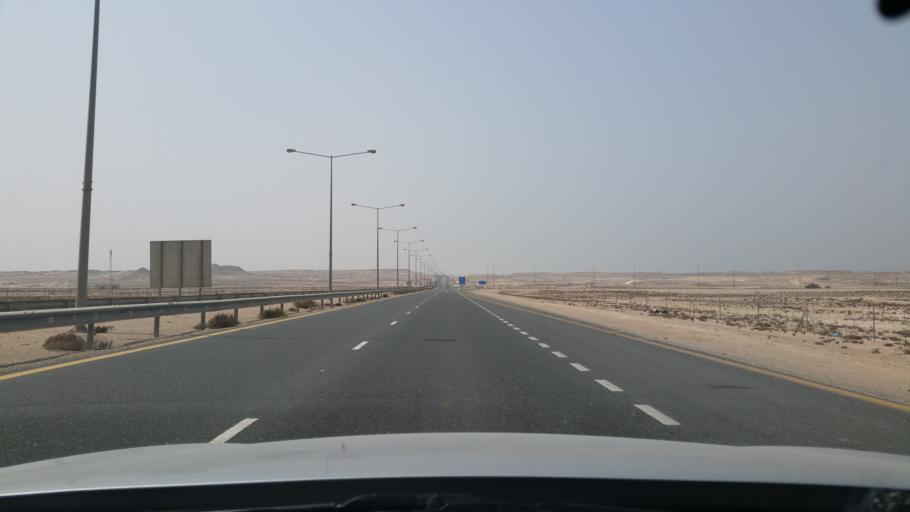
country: QA
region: Baladiyat ar Rayyan
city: Dukhan
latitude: 25.3751
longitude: 50.7808
